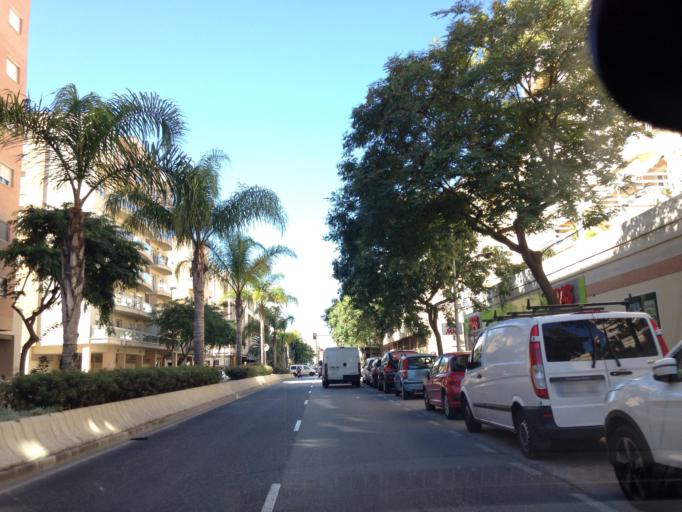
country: ES
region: Andalusia
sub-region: Provincia de Malaga
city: Malaga
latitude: 36.6948
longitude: -4.4417
